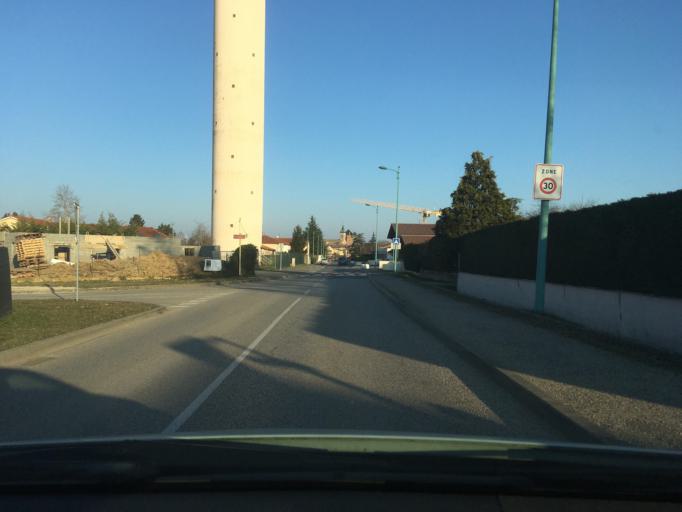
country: FR
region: Rhone-Alpes
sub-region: Departement de l'Ain
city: Amberieux-en-Dombes
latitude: 45.9928
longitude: 4.9083
